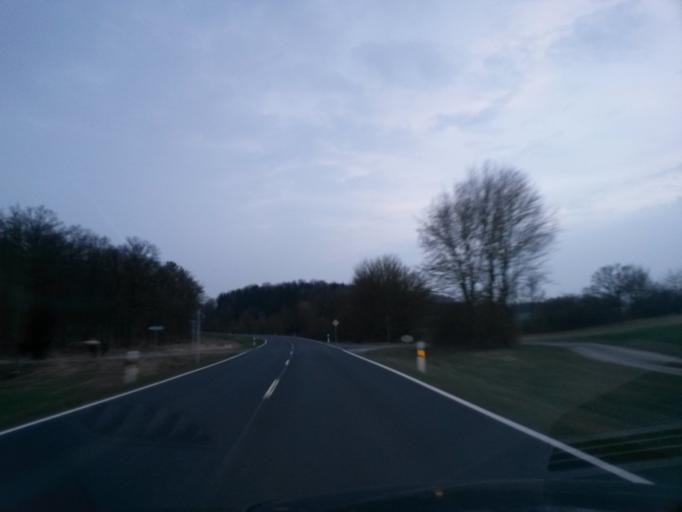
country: DE
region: Bavaria
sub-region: Regierungsbezirk Unterfranken
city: Sulzfeld
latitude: 50.2393
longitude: 10.3873
